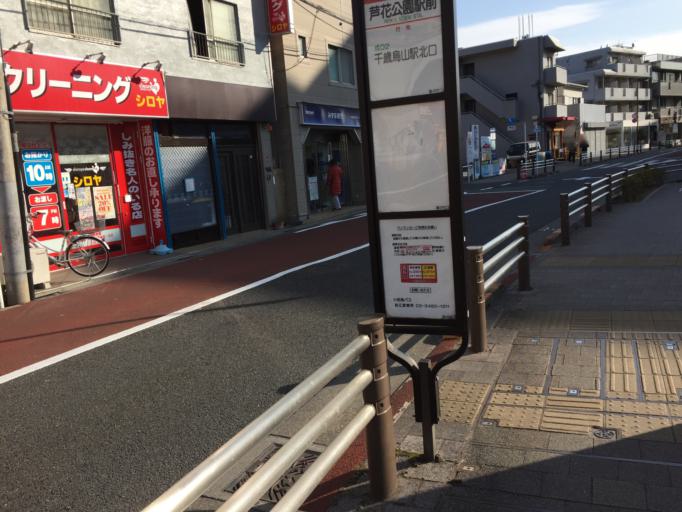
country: JP
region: Tokyo
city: Mitaka-shi
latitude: 35.6704
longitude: 139.6092
